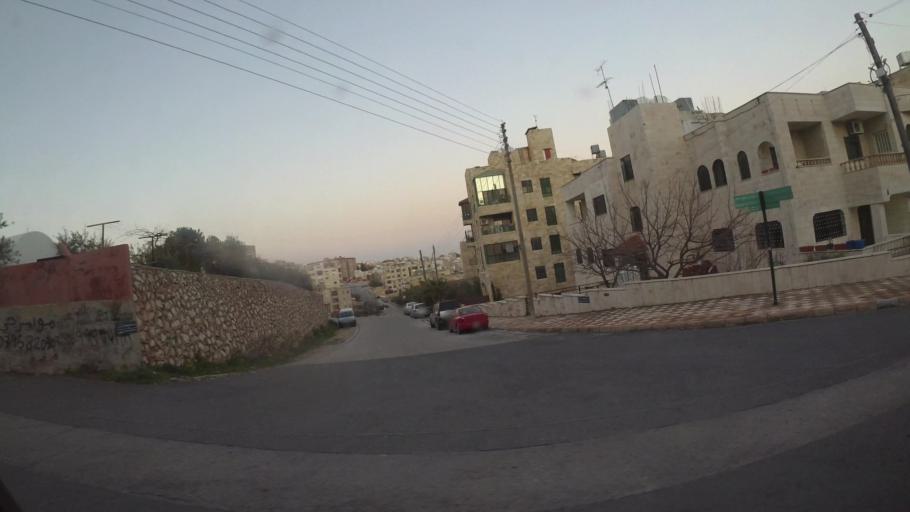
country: JO
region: Amman
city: Al Jubayhah
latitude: 31.9964
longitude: 35.8579
